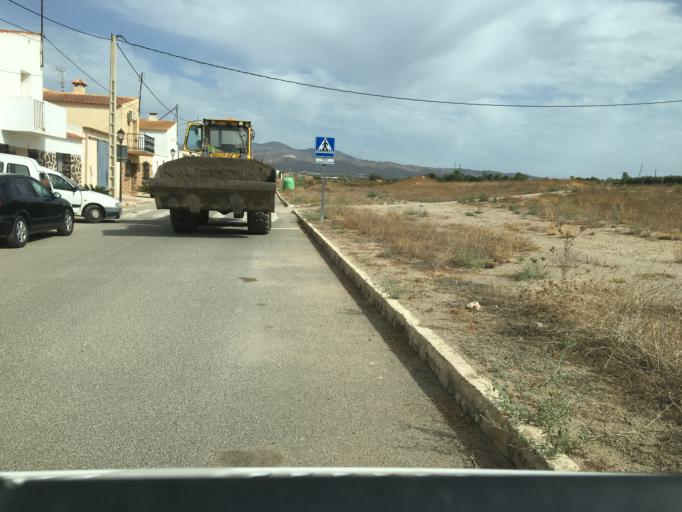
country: ES
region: Andalusia
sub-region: Provincia de Almeria
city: Huercal-Overa
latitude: 37.4209
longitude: -1.8770
